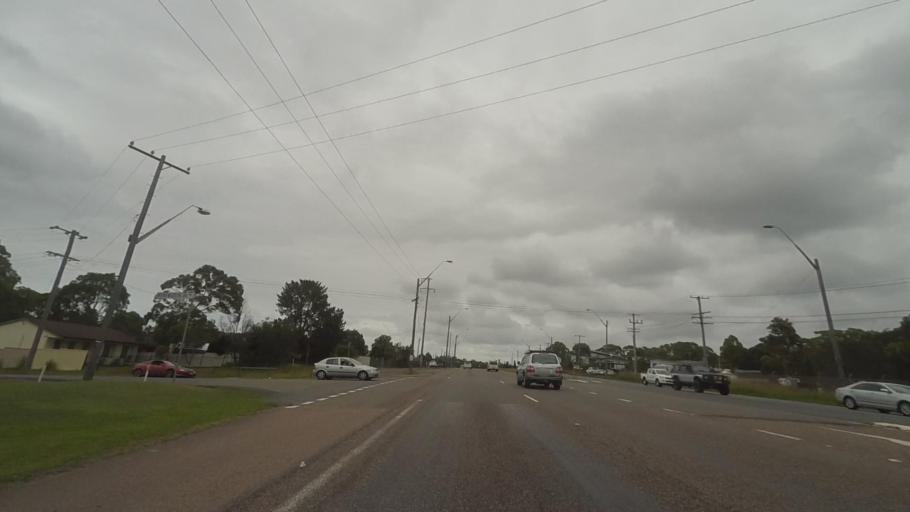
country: AU
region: New South Wales
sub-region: Wyong Shire
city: Buff Point
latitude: -33.1975
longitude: 151.5247
